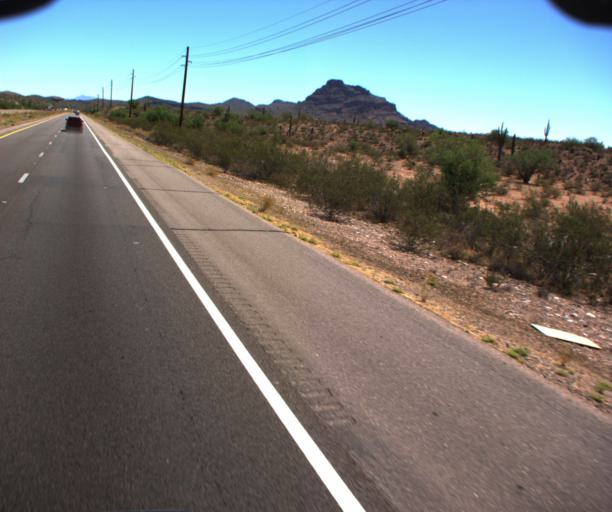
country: US
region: Arizona
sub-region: Maricopa County
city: Fountain Hills
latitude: 33.5227
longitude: -111.7397
